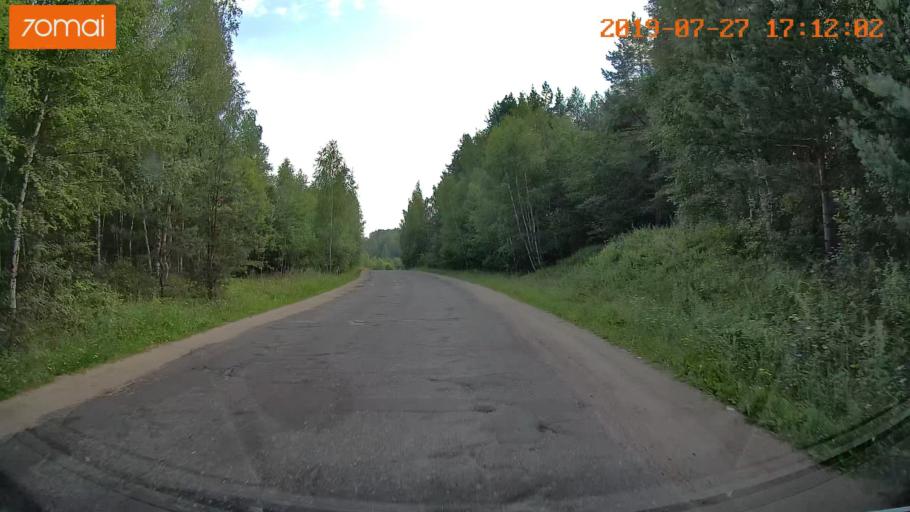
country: RU
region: Ivanovo
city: Novo-Talitsy
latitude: 57.0610
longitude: 40.8632
